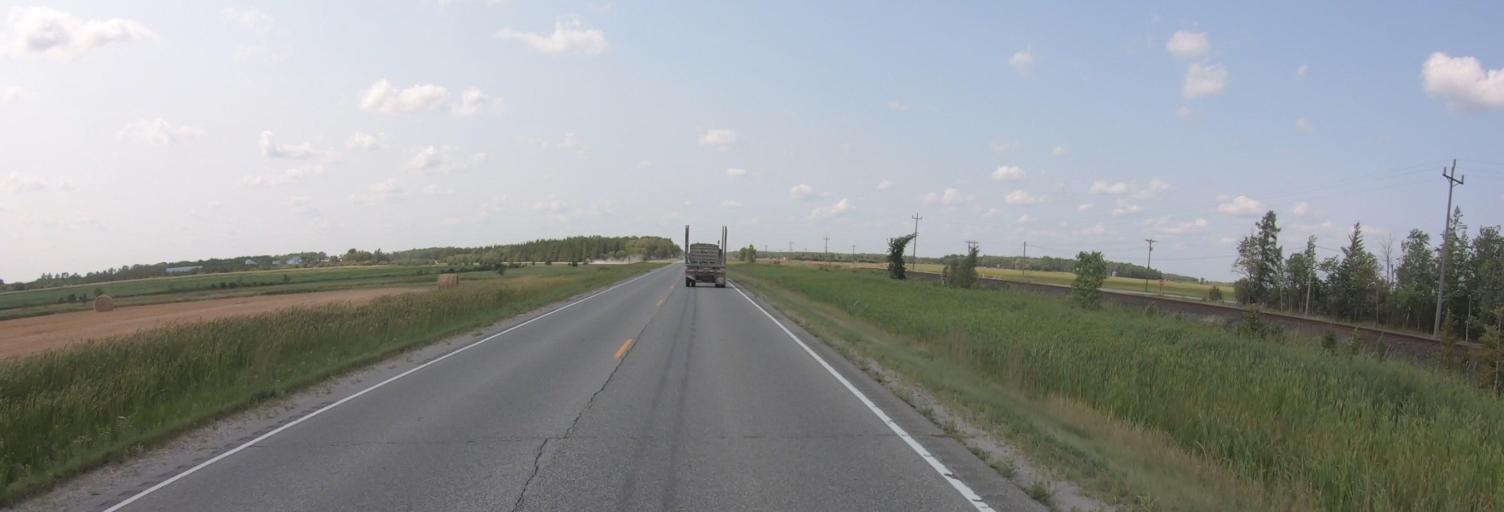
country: US
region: Minnesota
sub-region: Roseau County
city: Warroad
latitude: 48.8568
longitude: -95.2305
